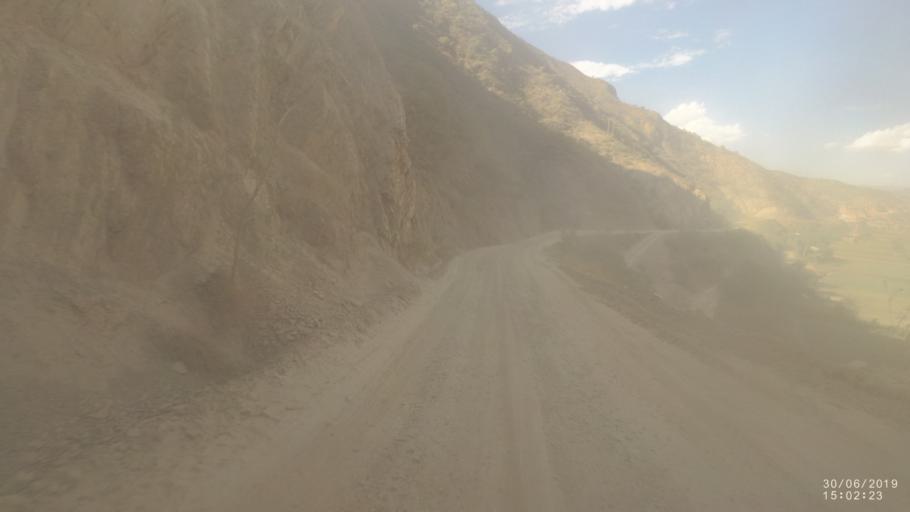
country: BO
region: Cochabamba
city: Irpa Irpa
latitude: -17.7325
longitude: -66.3327
